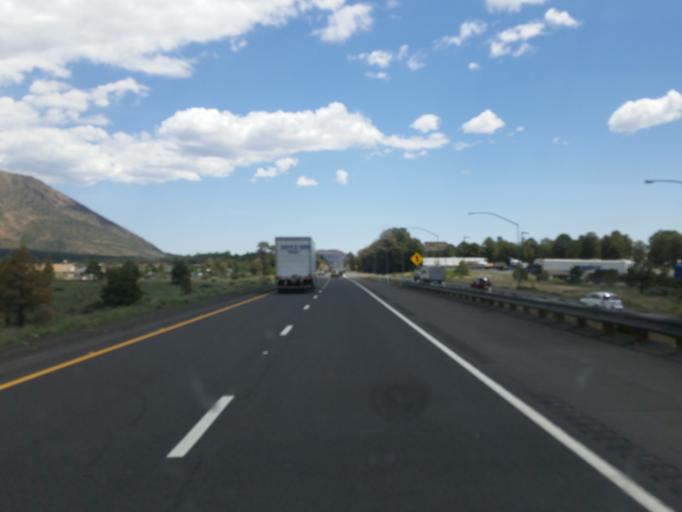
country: US
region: Arizona
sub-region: Coconino County
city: Flagstaff
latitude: 35.1926
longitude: -111.6200
